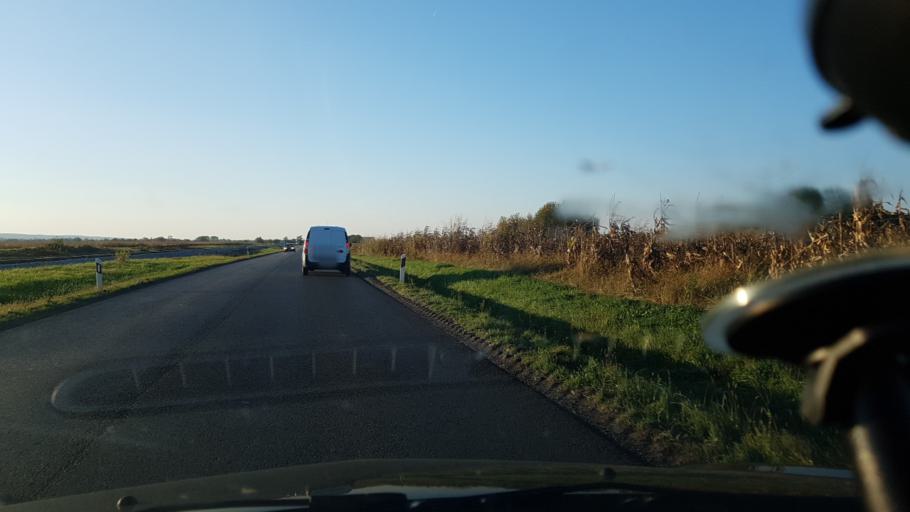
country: HR
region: Koprivnicko-Krizevacka
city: Virje
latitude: 46.0523
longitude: 17.0288
